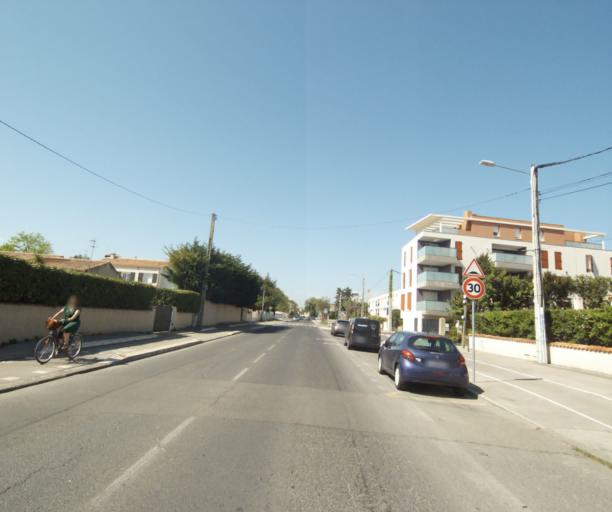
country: FR
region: Languedoc-Roussillon
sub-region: Departement de l'Herault
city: Castelnau-le-Lez
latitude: 43.6146
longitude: 3.8980
